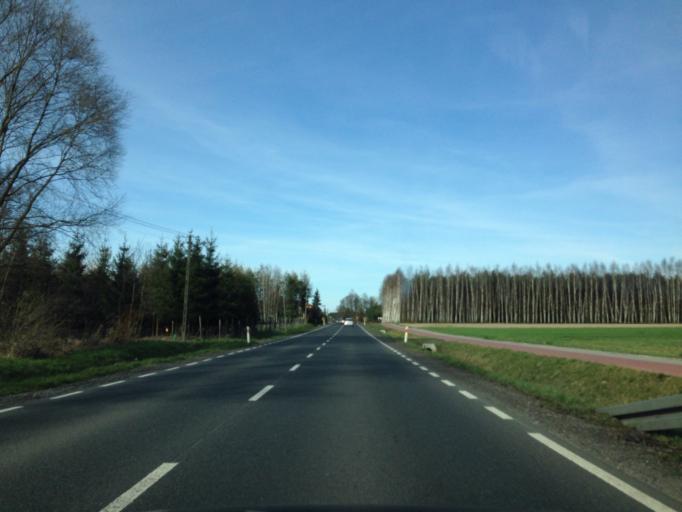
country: PL
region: Lodz Voivodeship
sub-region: Powiat poddebicki
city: Wartkowice
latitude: 51.9405
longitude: 18.9953
